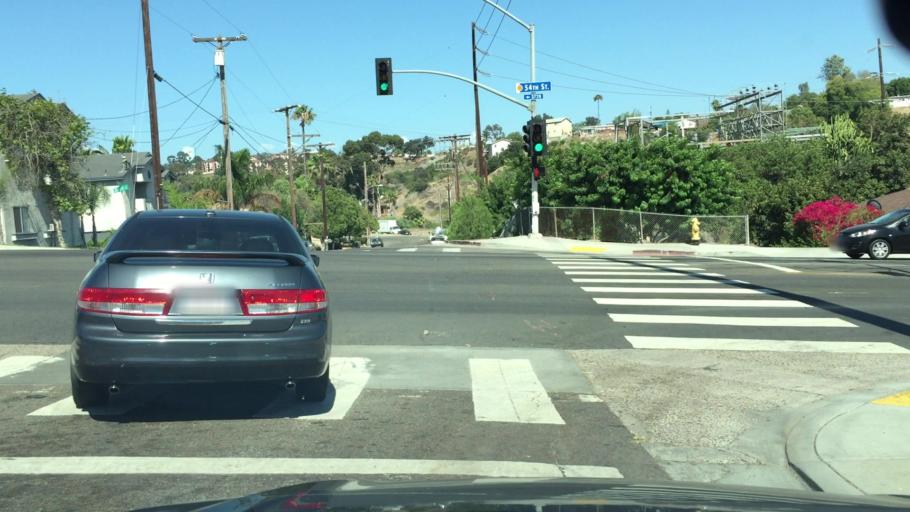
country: US
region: California
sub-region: San Diego County
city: Lemon Grove
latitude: 32.7458
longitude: -117.0797
